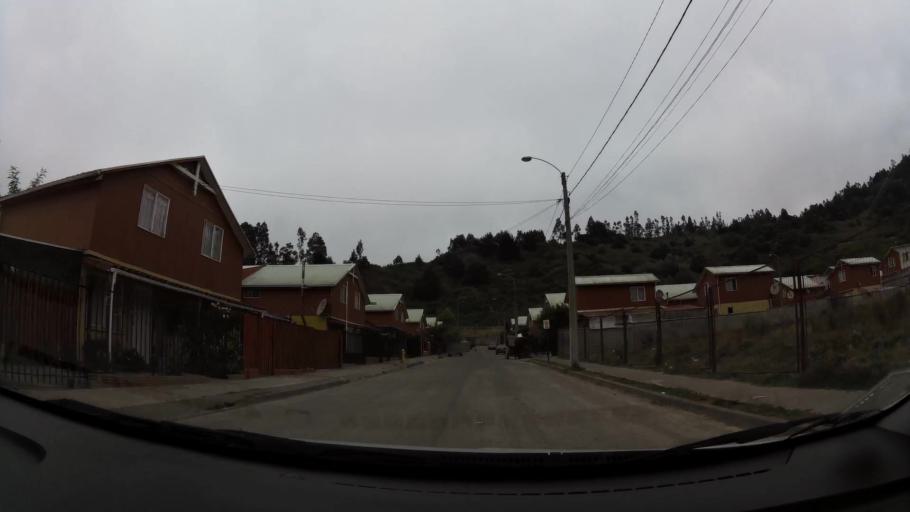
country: CL
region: Biobio
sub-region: Provincia de Concepcion
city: Concepcion
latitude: -36.8337
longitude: -73.0111
